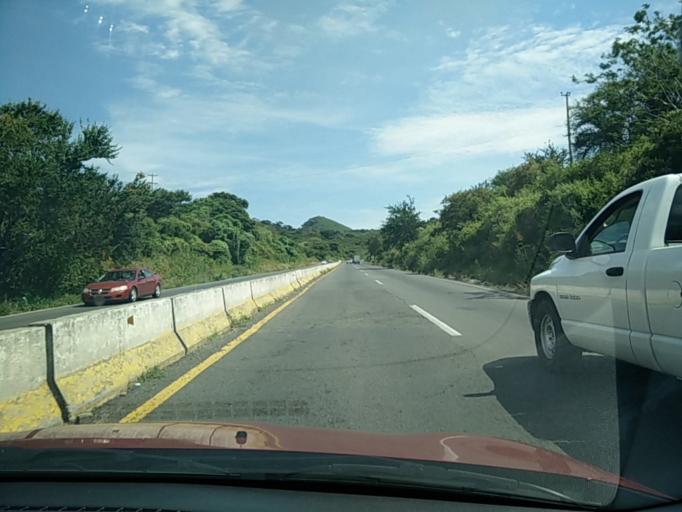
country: MX
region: Jalisco
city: Ixtlahuacan de los Membrillos
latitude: 20.3477
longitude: -103.1858
